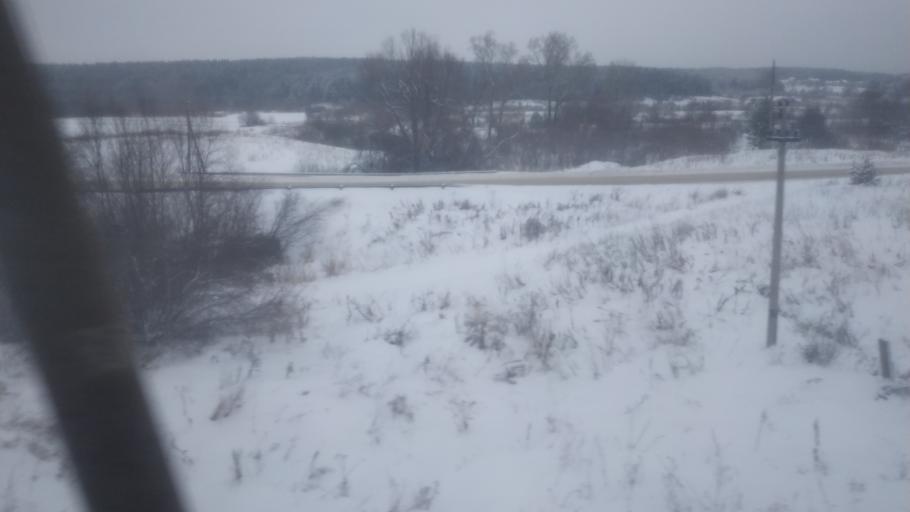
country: RU
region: Udmurtiya
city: Sigayevo
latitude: 56.4526
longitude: 53.6975
